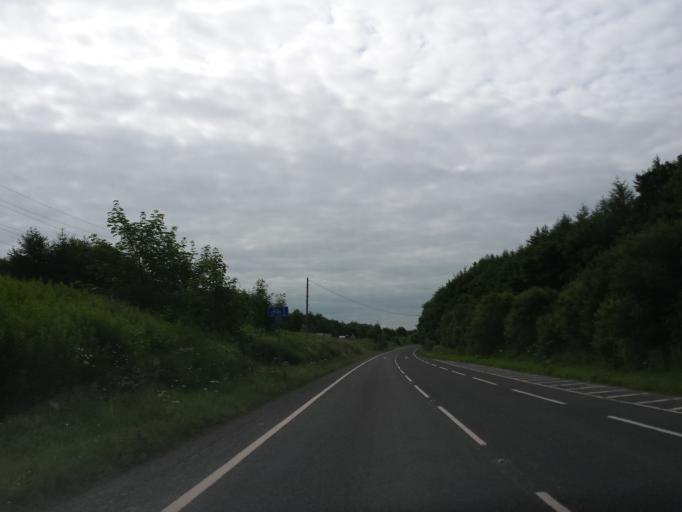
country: GB
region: Scotland
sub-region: Dumfries and Galloway
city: Moffat
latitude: 55.3247
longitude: -3.4703
